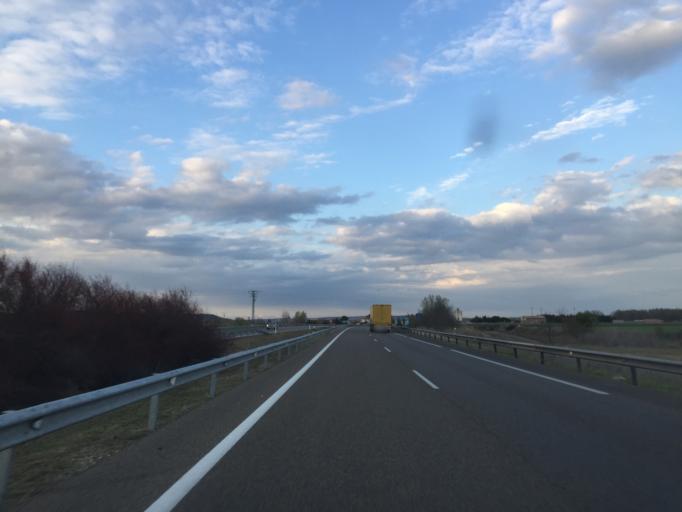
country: ES
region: Castille and Leon
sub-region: Provincia de Palencia
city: Torquemada
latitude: 42.0246
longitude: -4.3317
